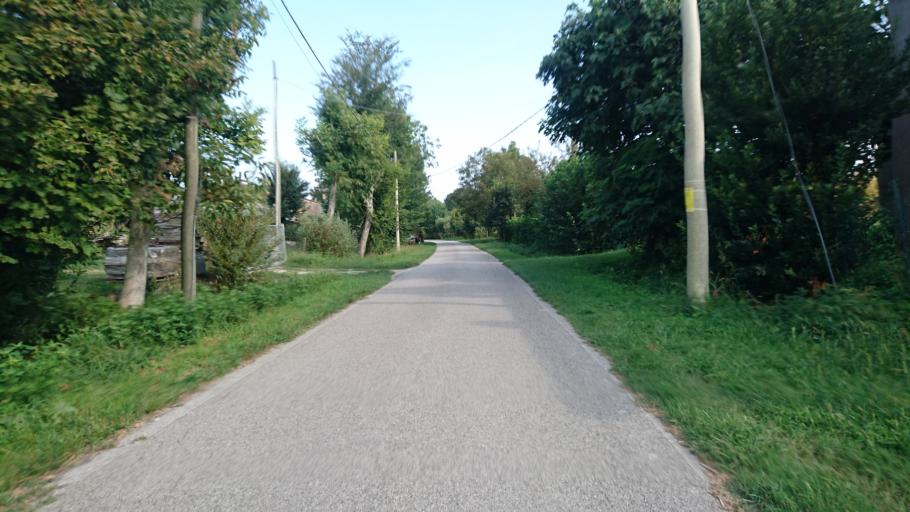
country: IT
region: Veneto
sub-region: Provincia di Padova
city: Selvazzano Dentro
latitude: 45.4001
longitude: 11.7883
